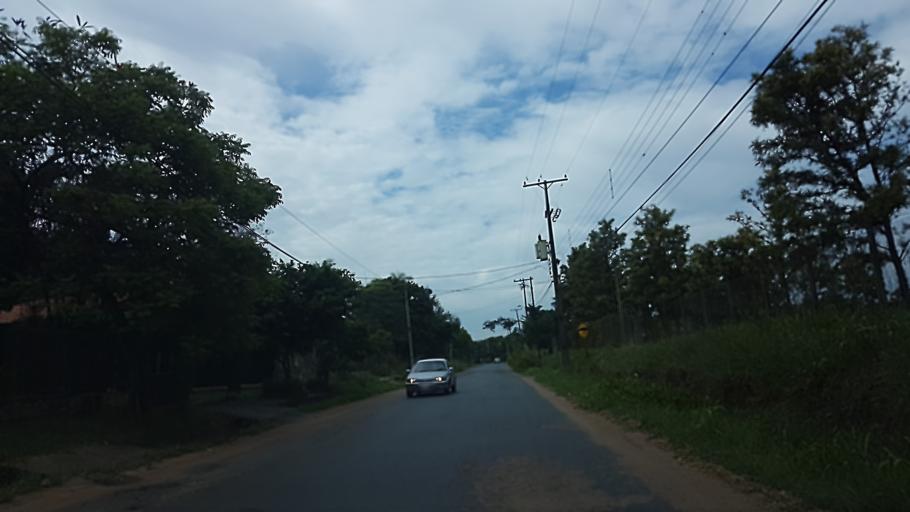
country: PY
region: Central
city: San Lorenzo
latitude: -25.2801
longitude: -57.4959
